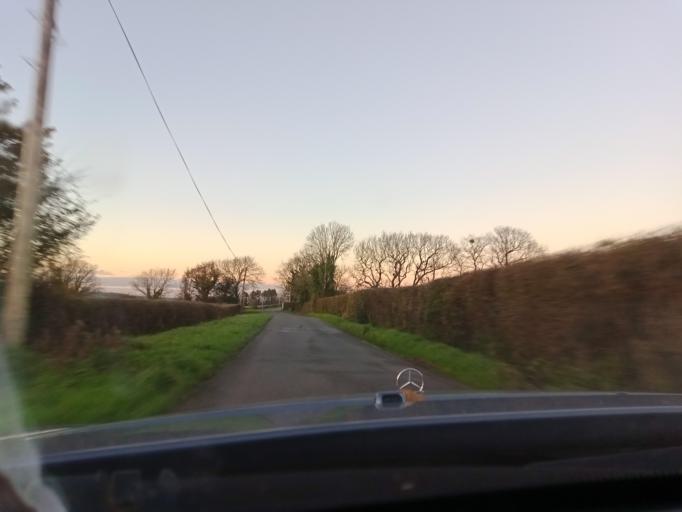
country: IE
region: Leinster
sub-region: Kilkenny
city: Thomastown
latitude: 52.4735
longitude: -7.0990
